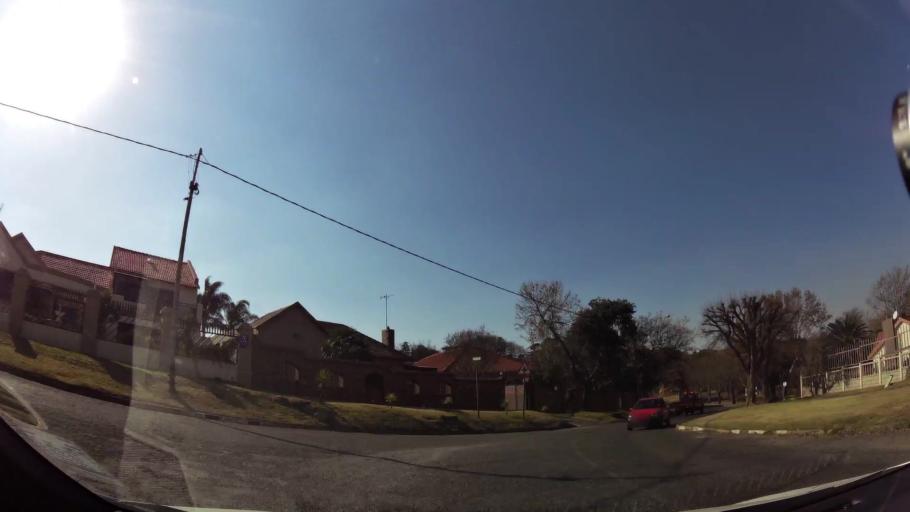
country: ZA
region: Gauteng
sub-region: City of Johannesburg Metropolitan Municipality
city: Johannesburg
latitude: -26.2615
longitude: 28.0690
